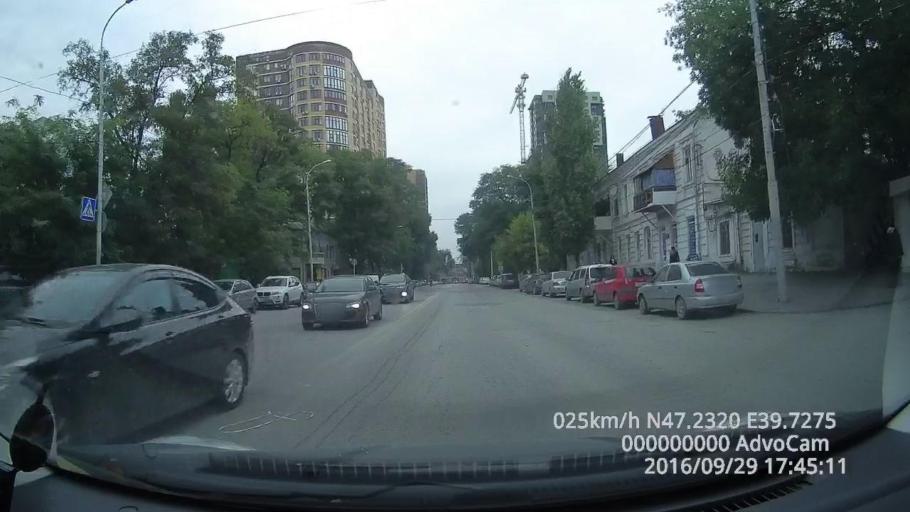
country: RU
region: Rostov
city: Rostov-na-Donu
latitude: 47.2320
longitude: 39.7275
